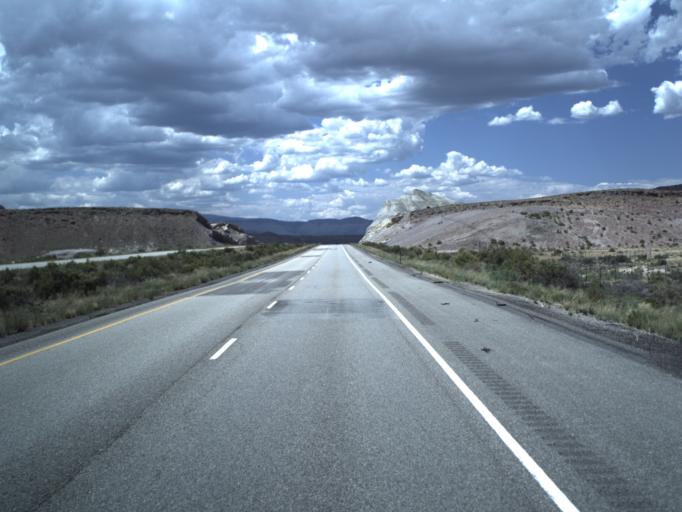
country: US
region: Utah
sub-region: Emery County
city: Ferron
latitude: 38.8180
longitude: -111.1658
